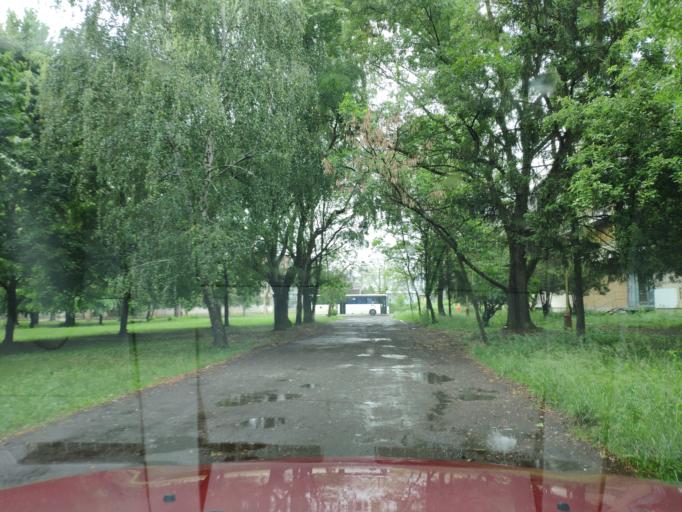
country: SK
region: Kosicky
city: Cierna nad Tisou
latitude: 48.4189
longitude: 22.0901
